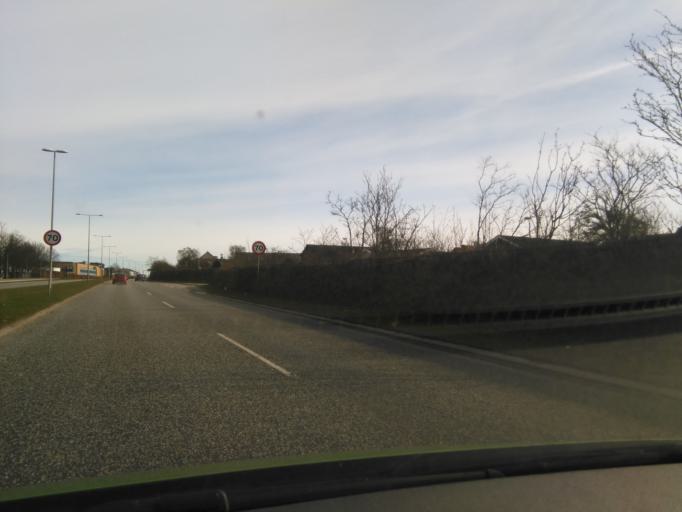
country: DK
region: Central Jutland
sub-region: Arhus Kommune
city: Arhus
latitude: 56.1804
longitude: 10.1899
